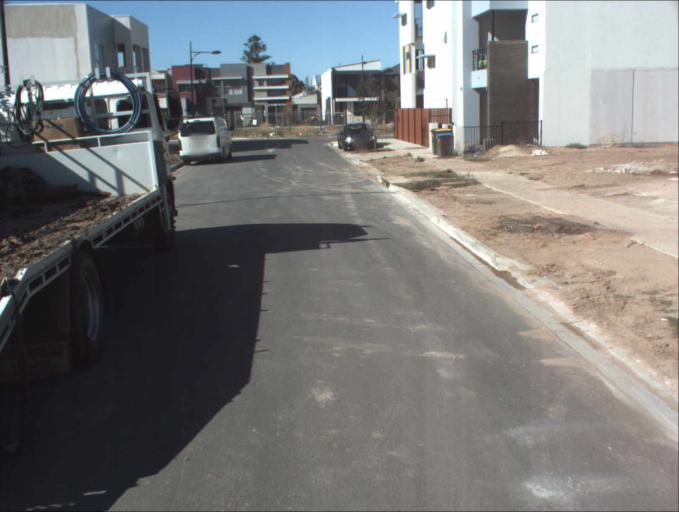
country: AU
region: South Australia
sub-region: Port Adelaide Enfield
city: Klemzig
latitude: -34.8641
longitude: 138.6258
